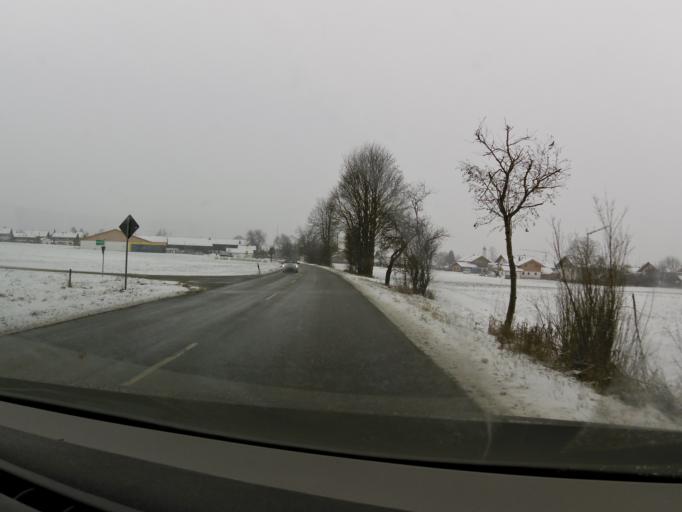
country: DE
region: Bavaria
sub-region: Upper Bavaria
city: Bichl
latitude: 47.7249
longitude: 11.4140
